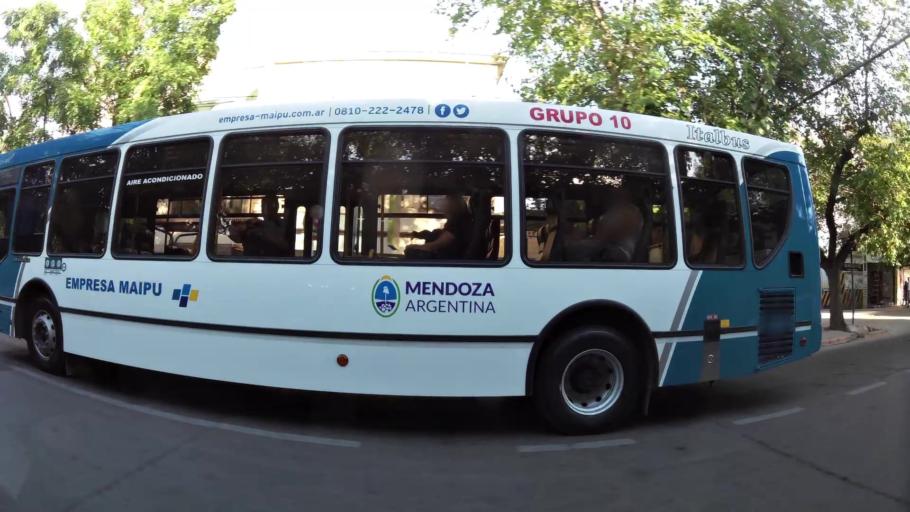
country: AR
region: Mendoza
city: Mendoza
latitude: -32.8968
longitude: -68.8384
